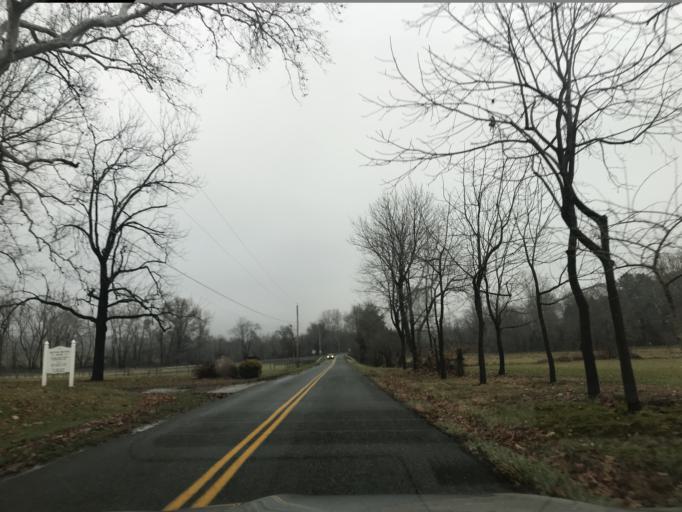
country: US
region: Maryland
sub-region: Harford County
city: South Bel Air
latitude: 39.5913
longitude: -76.2900
